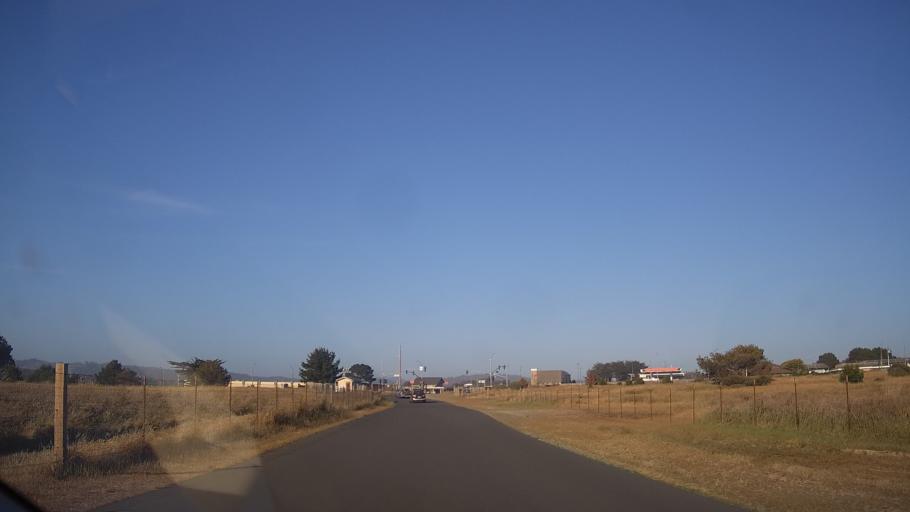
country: US
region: California
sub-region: Mendocino County
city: Fort Bragg
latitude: 39.4323
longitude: -123.8087
